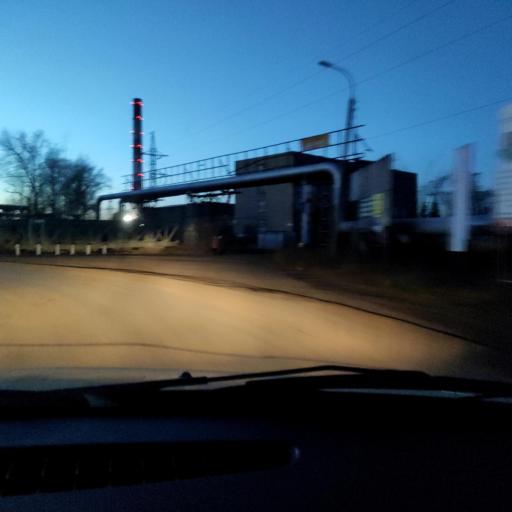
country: RU
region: Bashkortostan
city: Ufa
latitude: 54.8370
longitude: 56.0987
